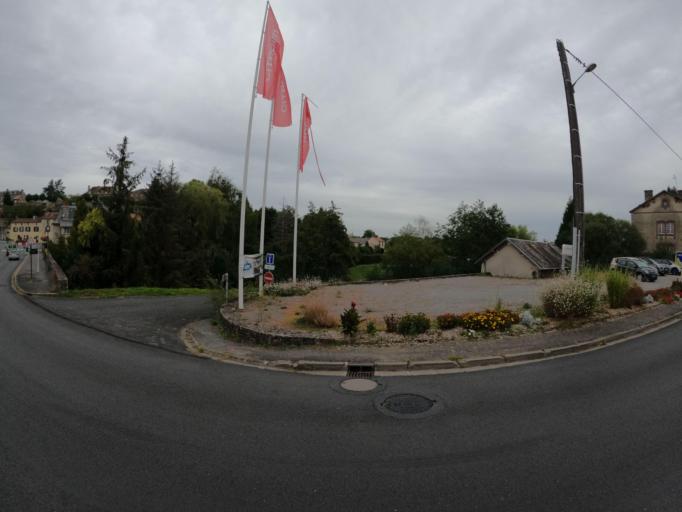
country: FR
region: Limousin
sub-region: Departement de la Haute-Vienne
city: Le Dorat
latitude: 46.2123
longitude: 1.0789
